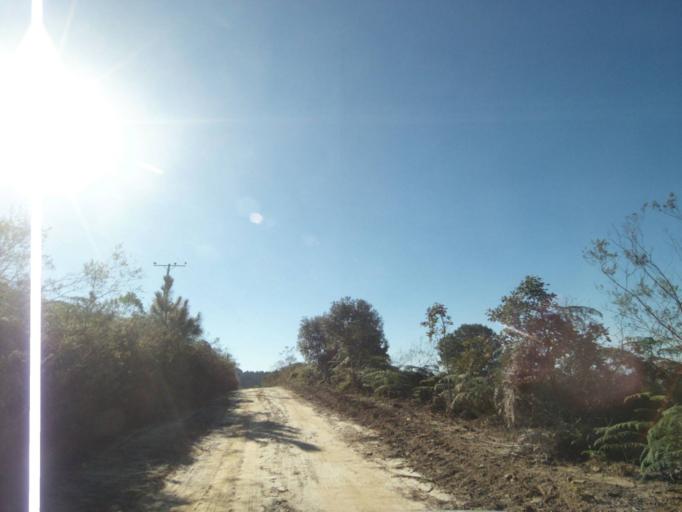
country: BR
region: Parana
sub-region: Tibagi
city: Tibagi
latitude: -24.5669
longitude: -50.4708
